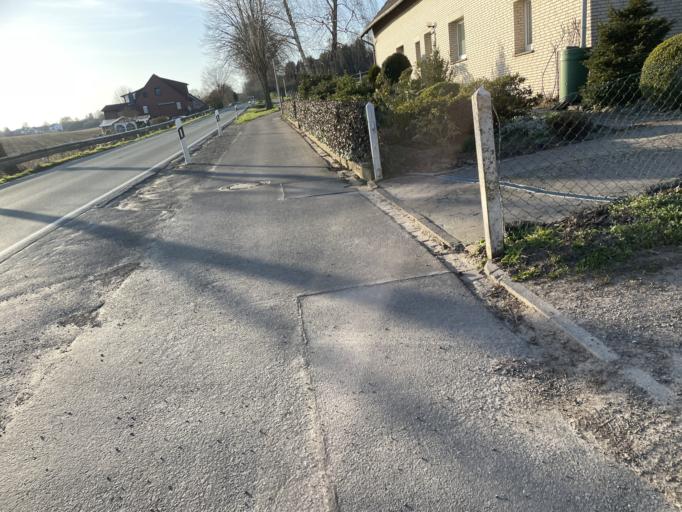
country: DE
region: North Rhine-Westphalia
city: Porta Westfalica
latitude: 52.2291
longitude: 8.9531
